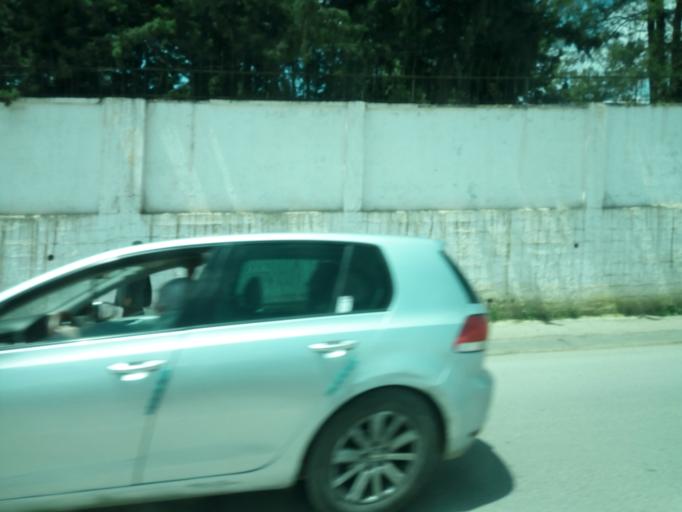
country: DZ
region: Tipaza
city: Saoula
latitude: 36.7257
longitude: 2.9901
